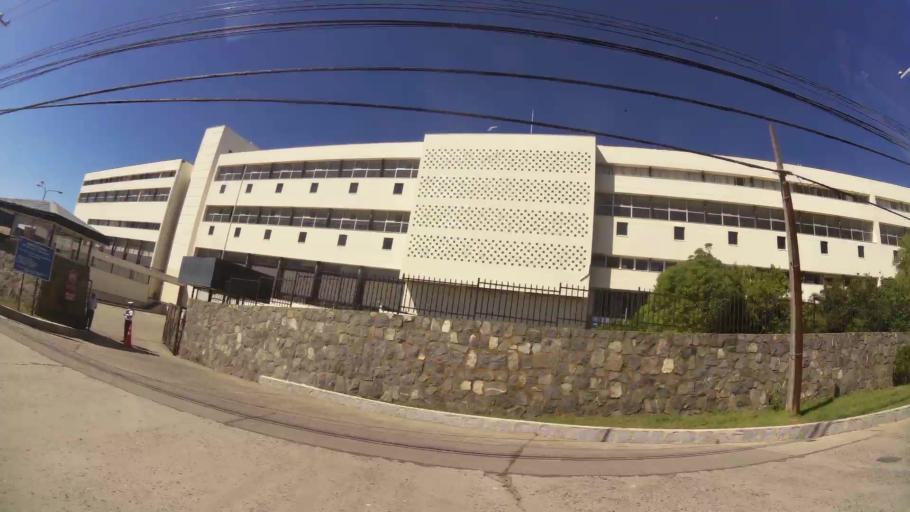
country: CL
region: Valparaiso
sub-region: Provincia de Valparaiso
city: Valparaiso
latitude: -33.0213
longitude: -71.6382
